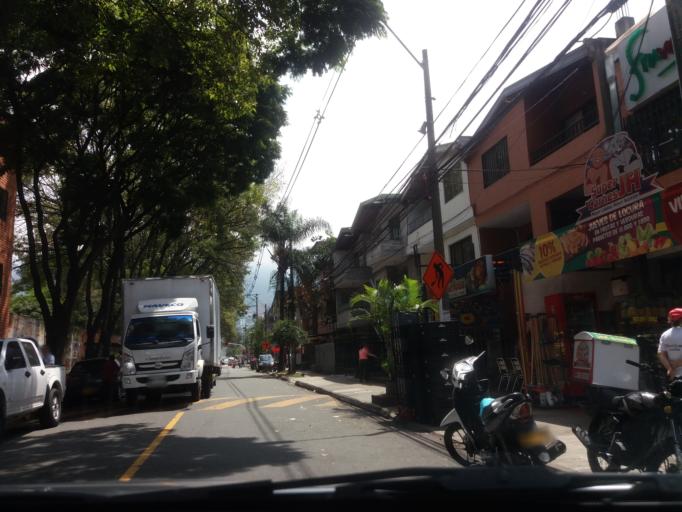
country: CO
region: Antioquia
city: Itagui
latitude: 6.2074
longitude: -75.5876
